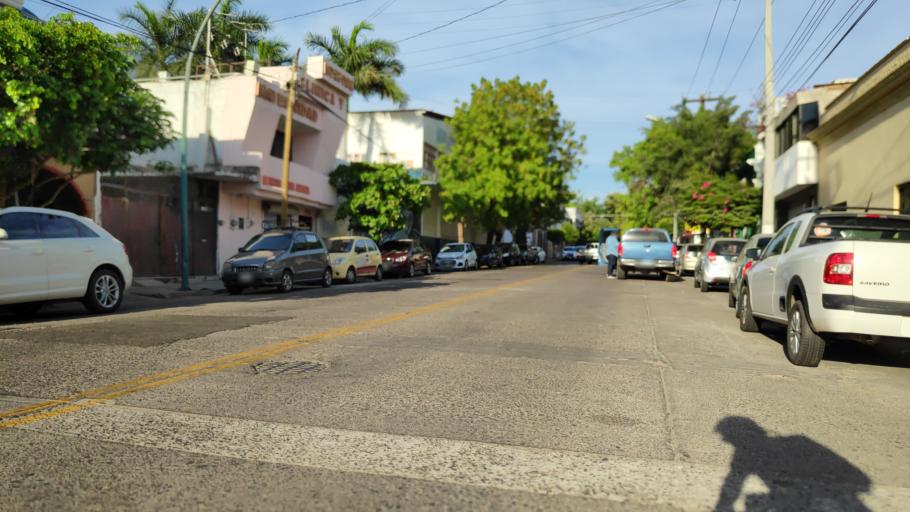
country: MX
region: Sinaloa
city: Culiacan
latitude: 24.8083
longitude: -107.4037
